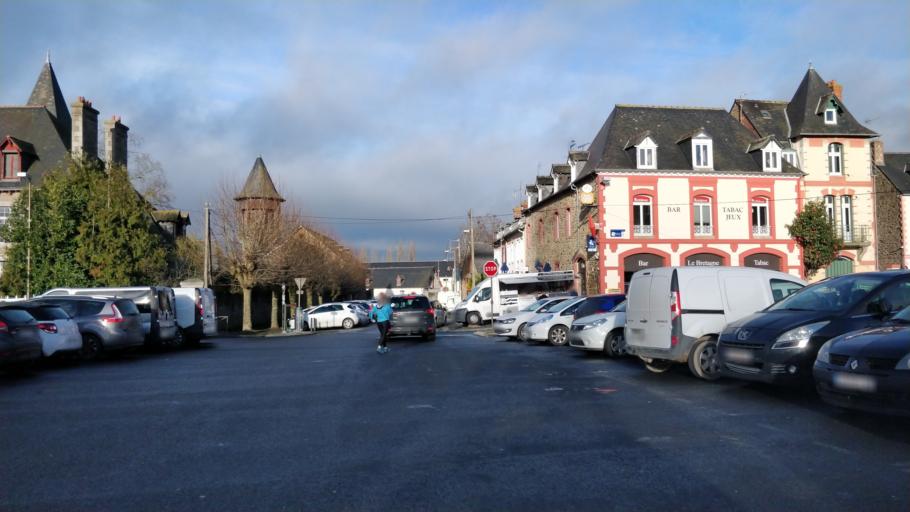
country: FR
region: Brittany
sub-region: Departement des Cotes-d'Armor
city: Lamballe
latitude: 48.4707
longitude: -2.5168
